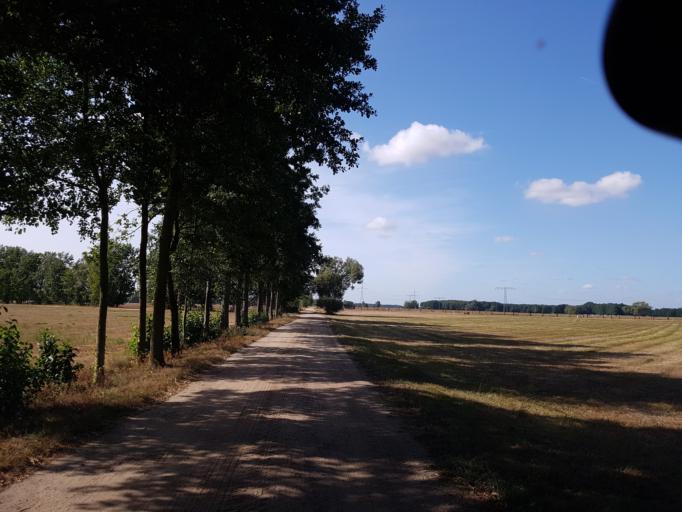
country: DE
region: Brandenburg
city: Sonnewalde
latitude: 51.6659
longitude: 13.6376
